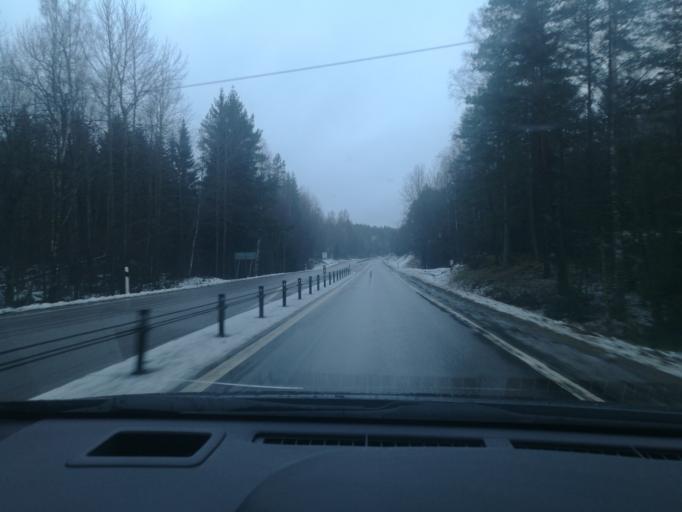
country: SE
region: OEstergoetland
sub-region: Norrkopings Kommun
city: Jursla
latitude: 58.7362
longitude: 16.1728
